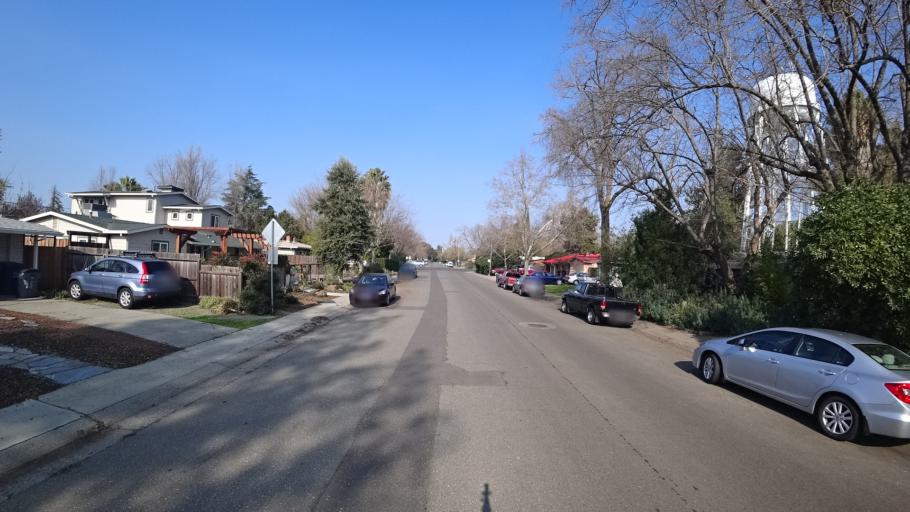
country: US
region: California
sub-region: Yolo County
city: Davis
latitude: 38.5499
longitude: -121.7565
